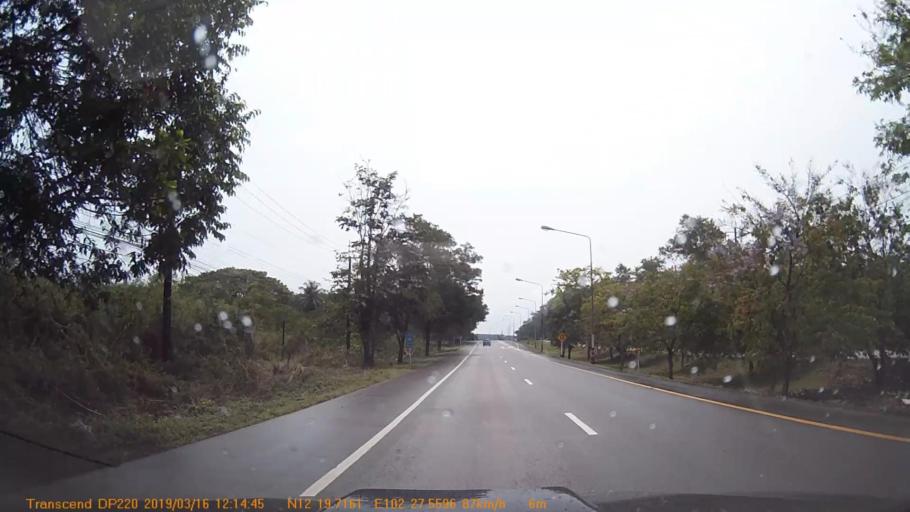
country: TH
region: Trat
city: Khao Saming
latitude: 12.3284
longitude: 102.4594
